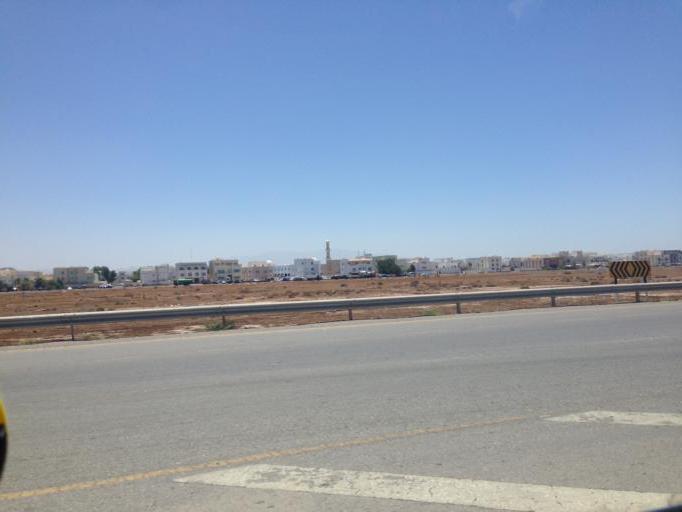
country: OM
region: Muhafazat Masqat
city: As Sib al Jadidah
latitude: 23.6270
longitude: 58.2606
